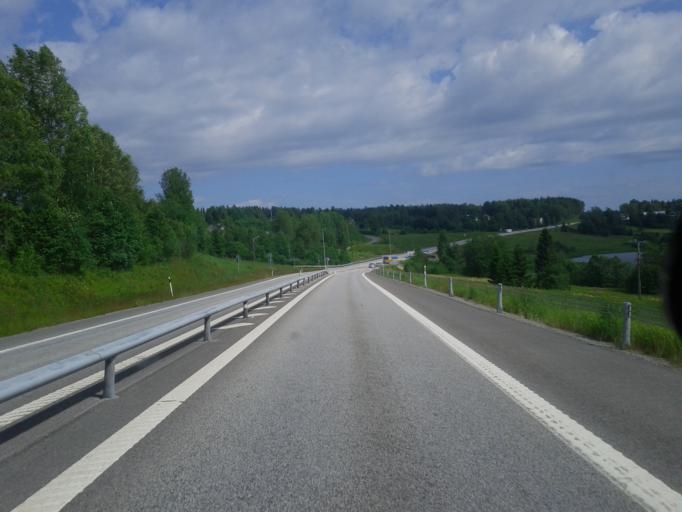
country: SE
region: Vaesternorrland
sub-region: OErnskoeldsviks Kommun
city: Ornskoldsvik
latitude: 63.3035
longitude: 18.9086
